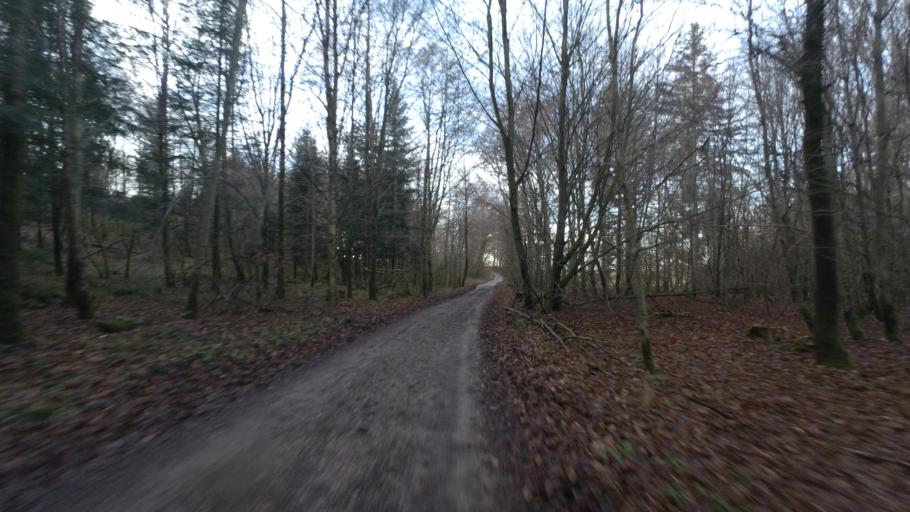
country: DE
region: Bavaria
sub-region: Upper Bavaria
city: Chieming
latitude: 47.8814
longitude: 12.5544
